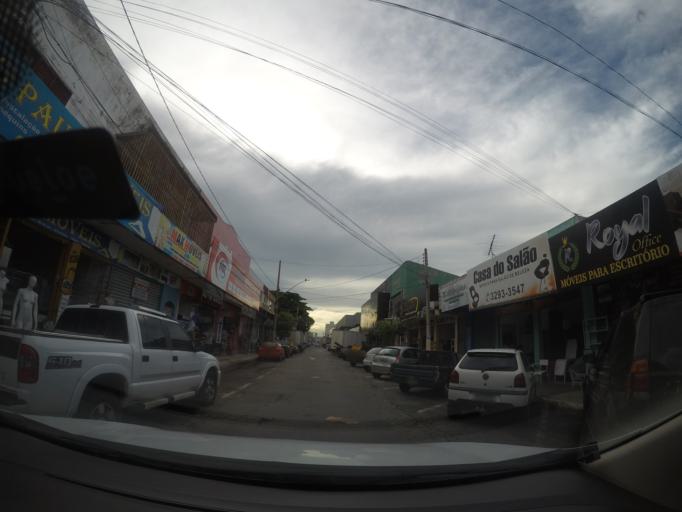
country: BR
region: Goias
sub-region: Goiania
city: Goiania
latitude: -16.6712
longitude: -49.2865
